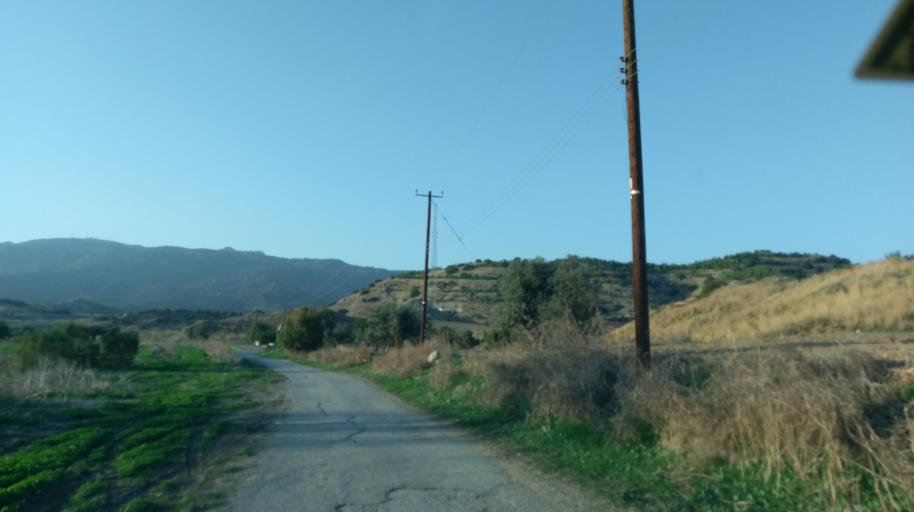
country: CY
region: Ammochostos
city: Trikomo
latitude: 35.3613
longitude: 33.9203
